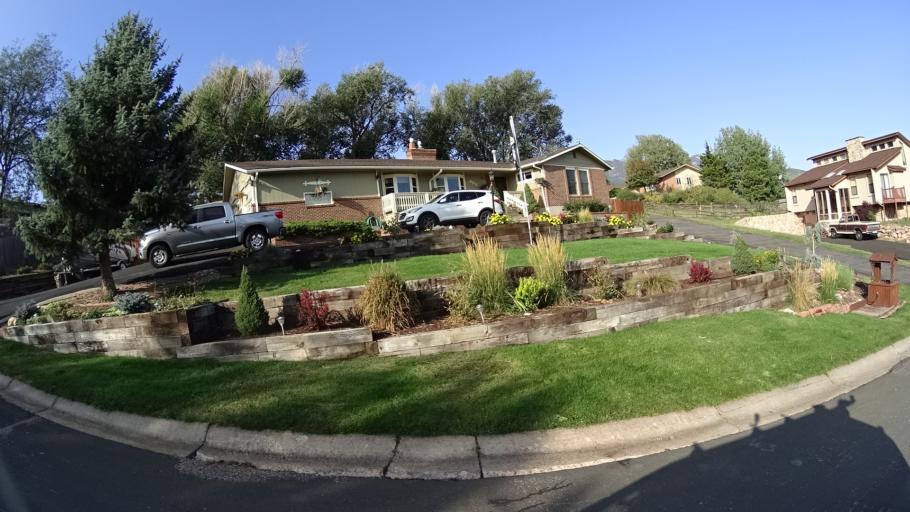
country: US
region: Colorado
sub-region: El Paso County
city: Colorado Springs
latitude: 38.8171
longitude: -104.8535
